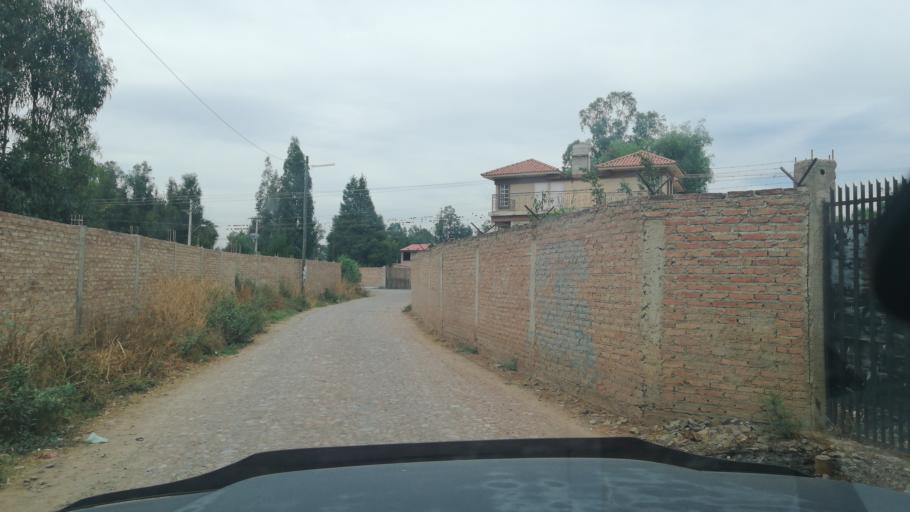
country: BO
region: Cochabamba
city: Cochabamba
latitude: -17.3633
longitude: -66.2209
